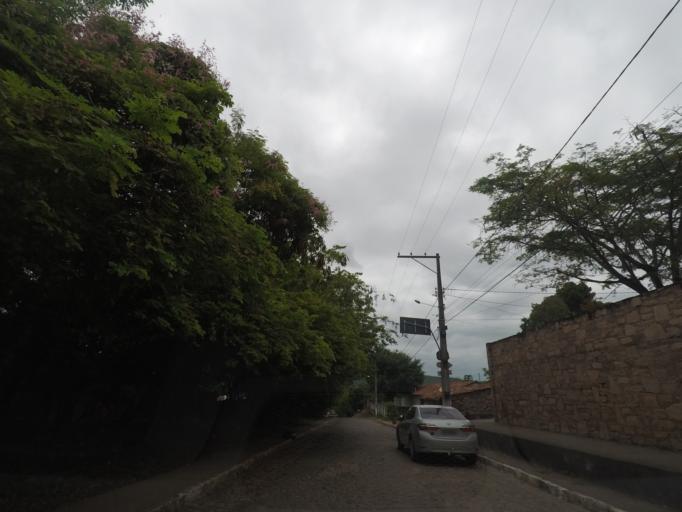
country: BR
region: Bahia
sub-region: Andarai
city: Vera Cruz
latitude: -12.5650
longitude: -41.3929
